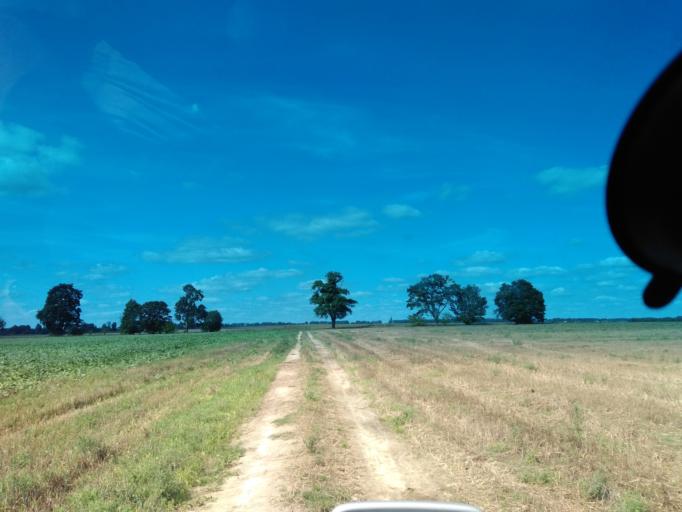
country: BY
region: Minsk
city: Stan'kava
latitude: 53.6329
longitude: 27.3259
